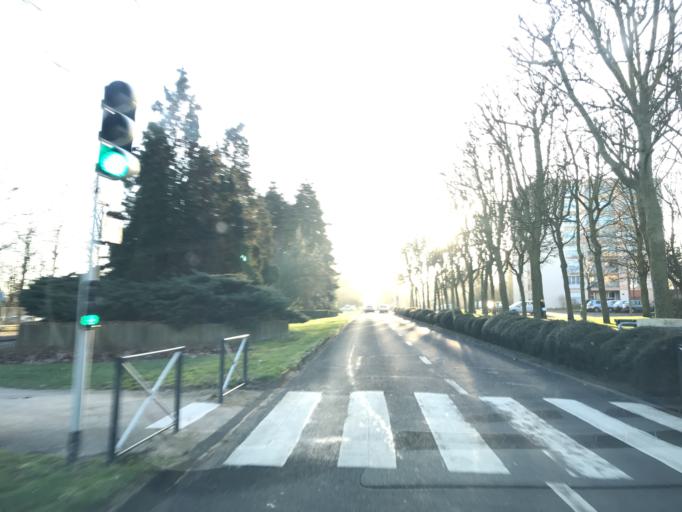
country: FR
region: Haute-Normandie
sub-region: Departement de la Seine-Maritime
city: Le Grand-Quevilly
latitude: 49.4062
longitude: 1.0512
